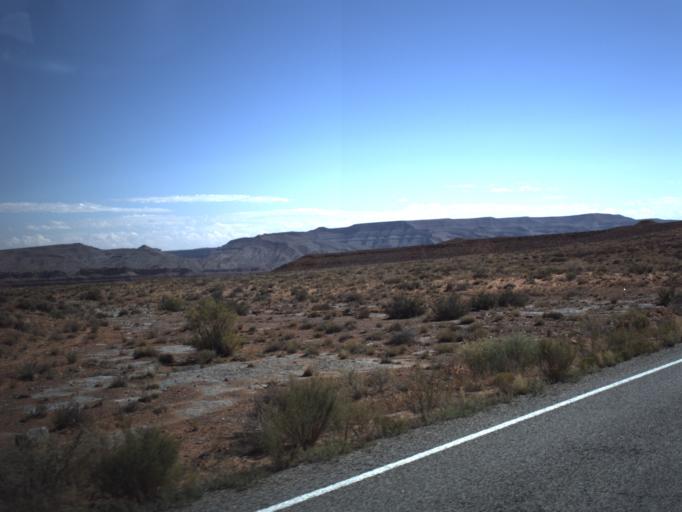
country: US
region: Utah
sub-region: San Juan County
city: Blanding
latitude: 37.2178
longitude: -109.8886
